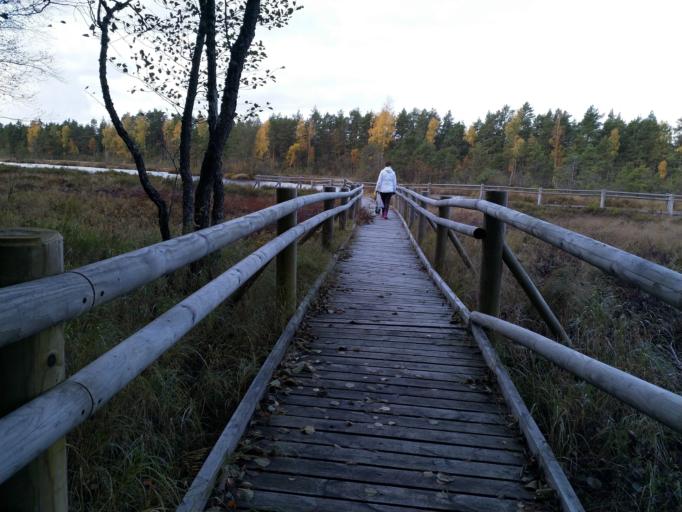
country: LV
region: Dundaga
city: Dundaga
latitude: 57.6500
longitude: 22.2552
